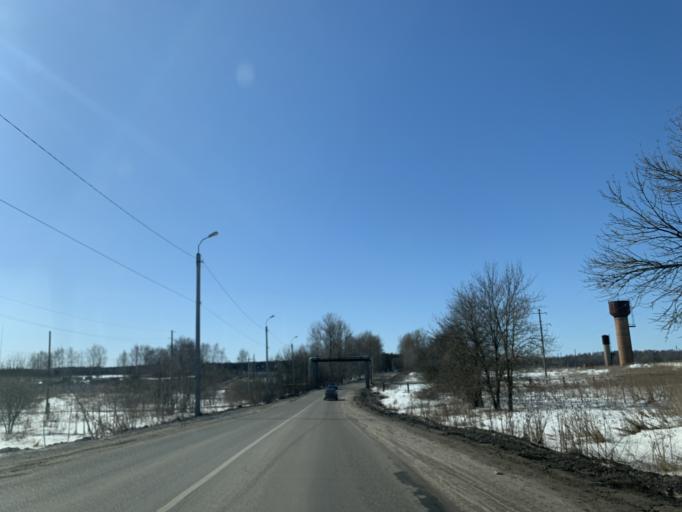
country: RU
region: Jaroslavl
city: Konstantinovskiy
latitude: 57.8371
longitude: 39.5640
